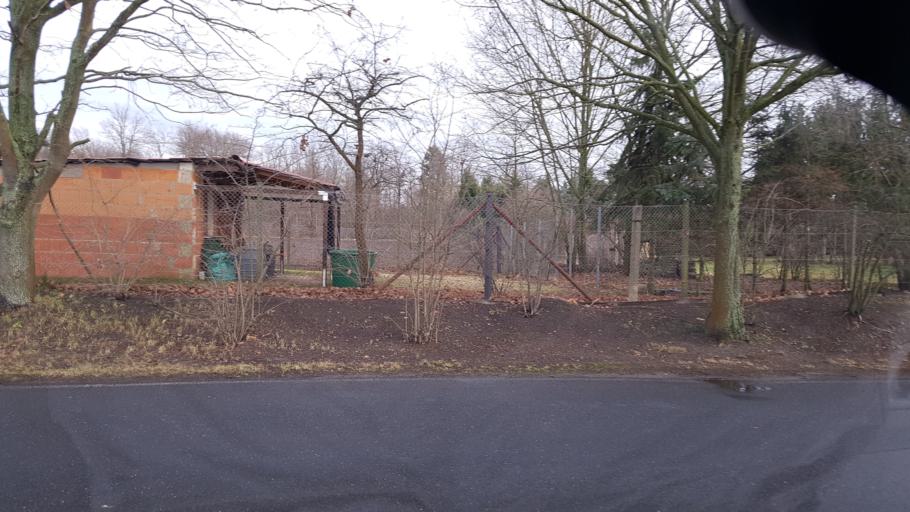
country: DE
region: Brandenburg
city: Altdobern
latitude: 51.6550
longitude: 13.9975
